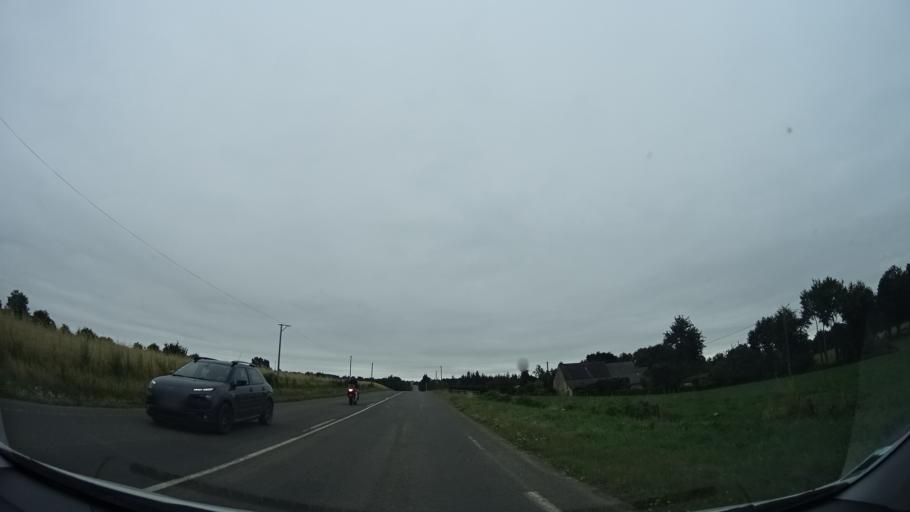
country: FR
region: Brittany
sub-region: Departement d'Ille-et-Vilaine
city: La Meziere
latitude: 48.2382
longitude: -1.7607
